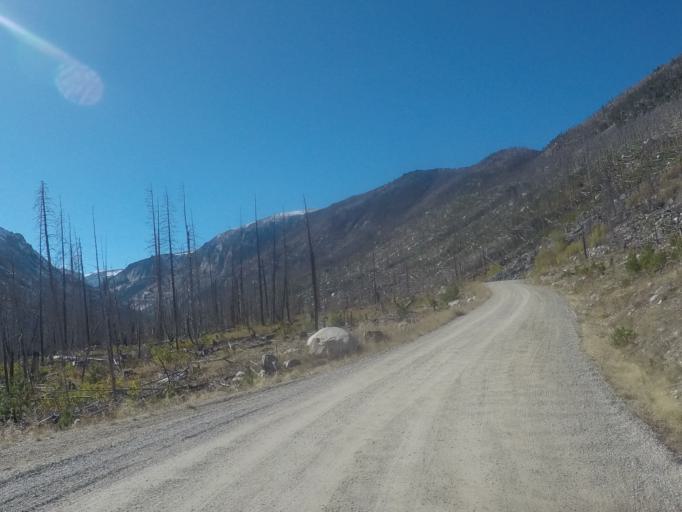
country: US
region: Montana
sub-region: Carbon County
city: Red Lodge
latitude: 45.1714
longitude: -109.4816
